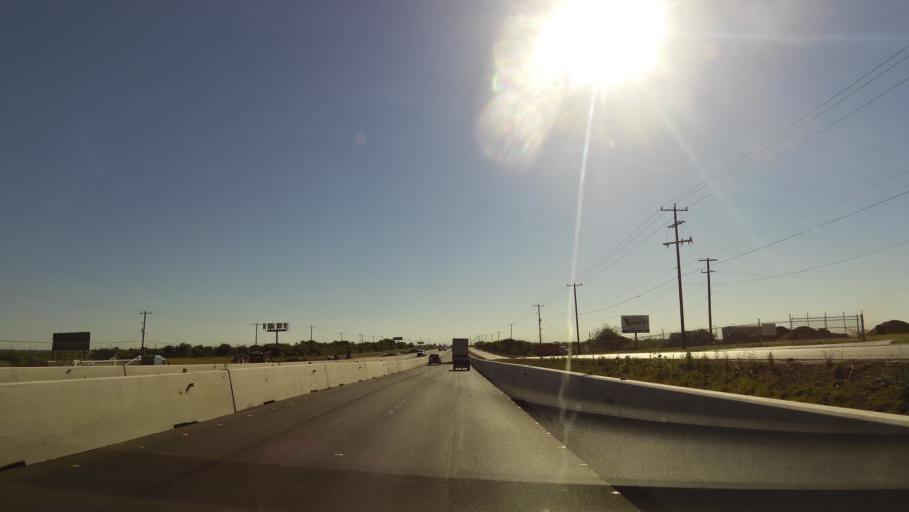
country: US
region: Texas
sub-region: Bexar County
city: Kirby
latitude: 29.4507
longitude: -98.3424
